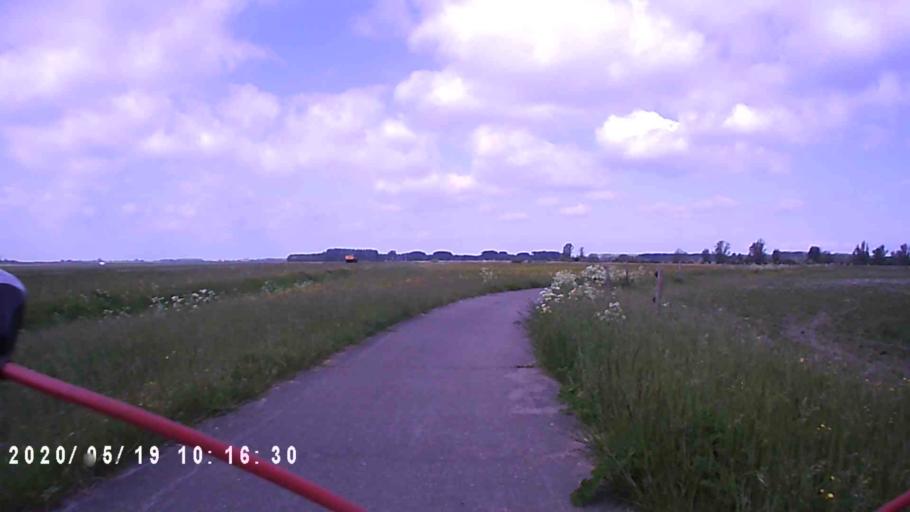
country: NL
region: Friesland
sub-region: Gemeente Kollumerland en Nieuwkruisland
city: Kollum
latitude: 53.3215
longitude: 6.2125
